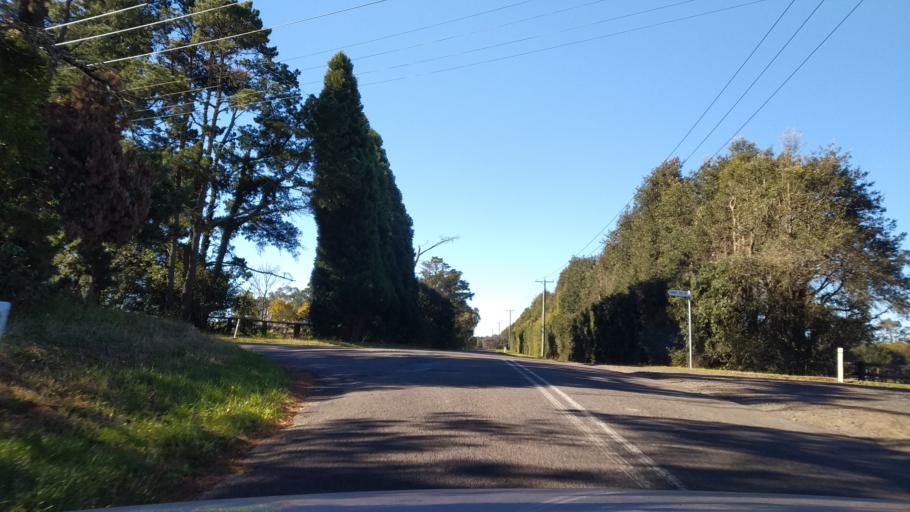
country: AU
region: New South Wales
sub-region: Wyong Shire
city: Little Jilliby
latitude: -33.2386
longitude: 151.2311
